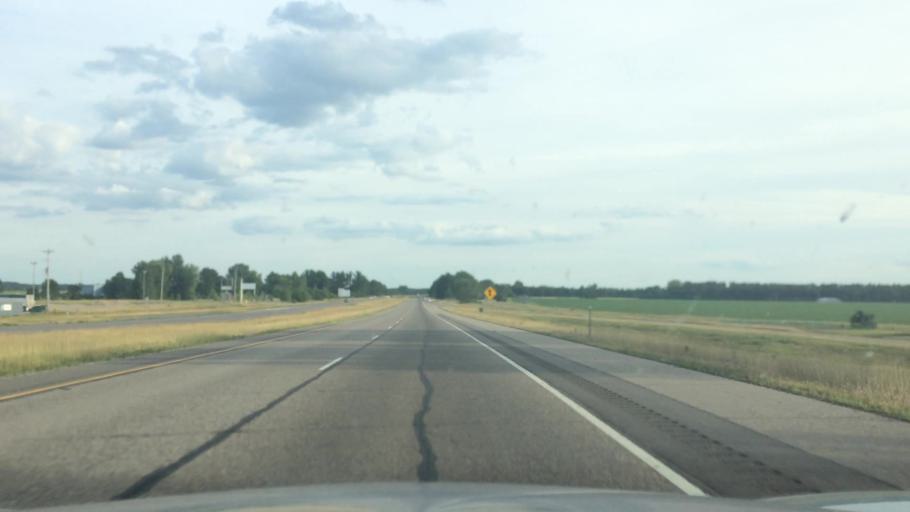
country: US
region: Wisconsin
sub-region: Portage County
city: Plover
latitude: 44.2128
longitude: -89.5247
